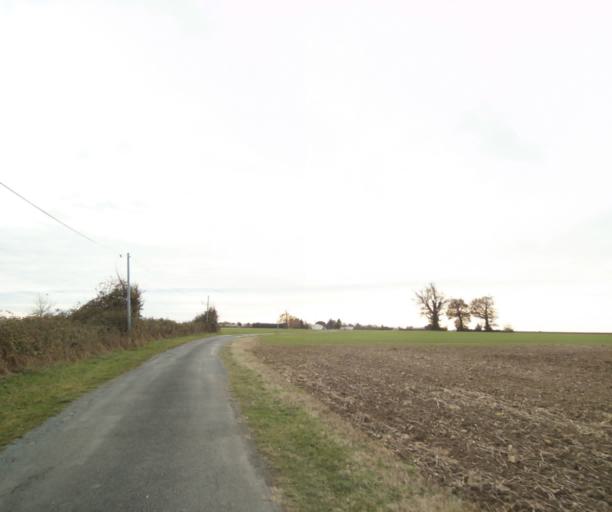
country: FR
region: Poitou-Charentes
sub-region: Departement de la Charente-Maritime
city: Corme-Royal
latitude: 45.7552
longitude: -0.8087
